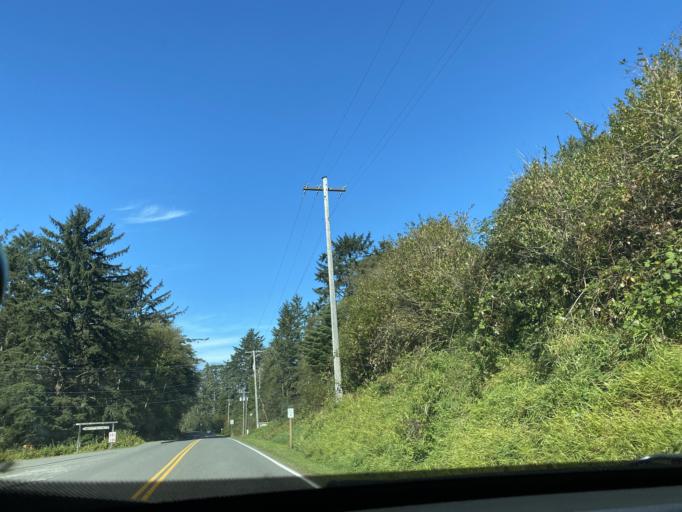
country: US
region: Washington
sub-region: Clallam County
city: Forks
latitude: 47.9039
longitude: -124.6292
